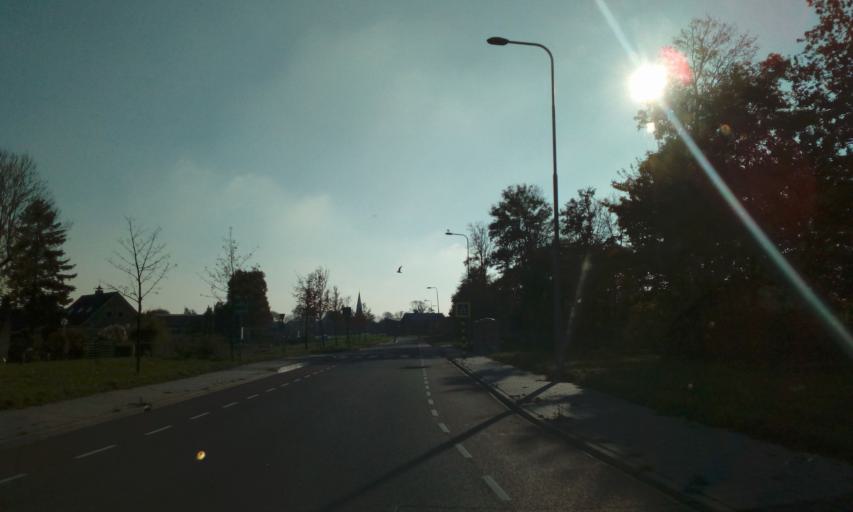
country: NL
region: South Holland
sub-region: Gemeente Lansingerland
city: Bleiswijk
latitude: 52.0181
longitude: 4.5805
